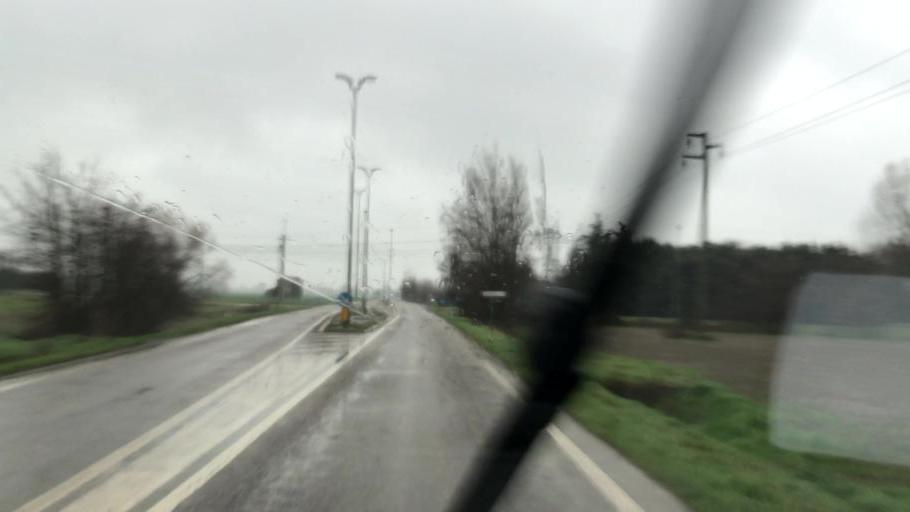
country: IT
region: Lombardy
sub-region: Provincia di Mantova
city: Carbonara di Po
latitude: 45.0207
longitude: 11.2531
